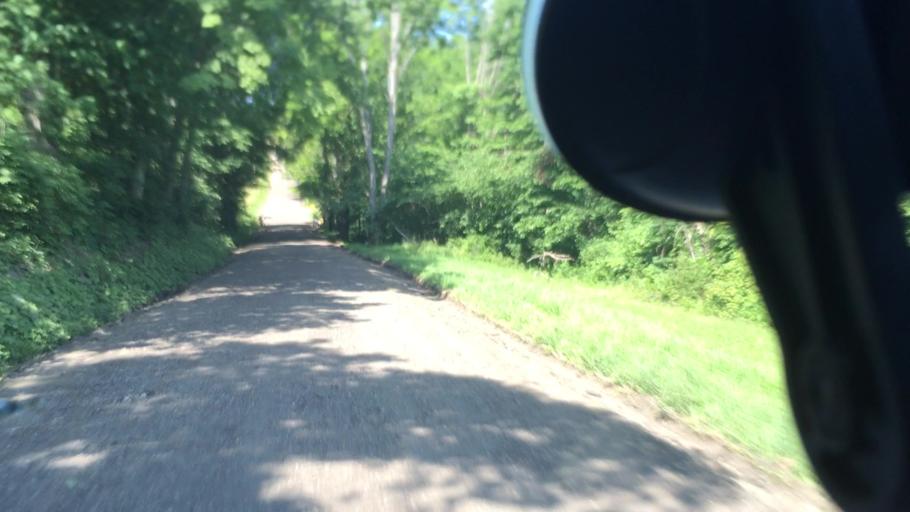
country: US
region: Ohio
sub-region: Columbiana County
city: Lisbon
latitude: 40.7627
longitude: -80.7880
